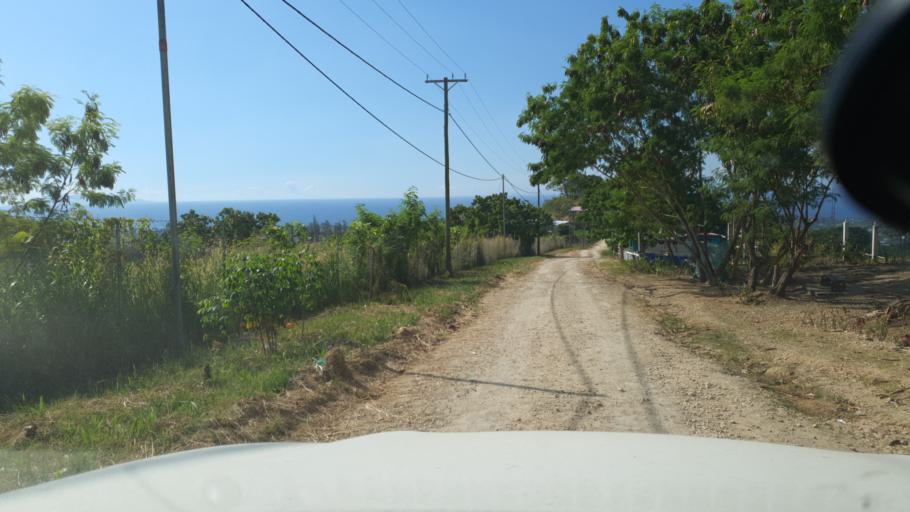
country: SB
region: Guadalcanal
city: Honiara
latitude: -9.4614
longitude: 159.9756
